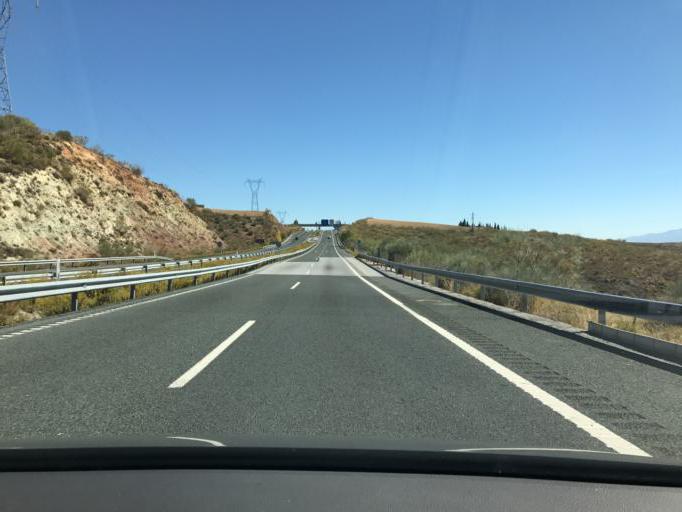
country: ES
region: Andalusia
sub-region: Provincia de Granada
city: Diezma
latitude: 37.3153
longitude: -3.3429
